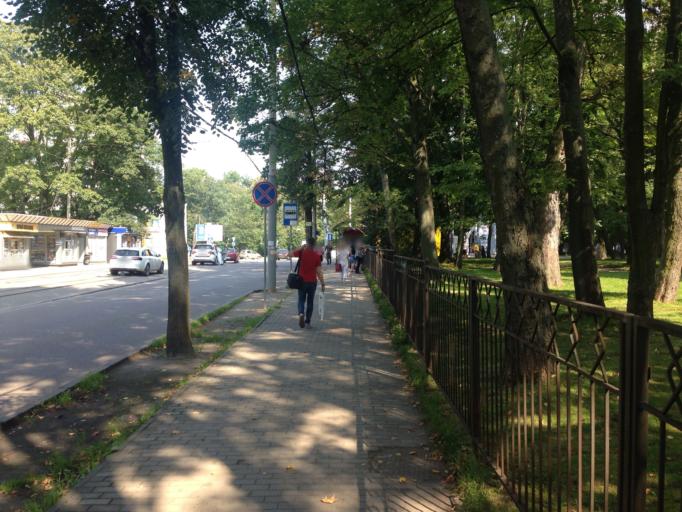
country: RU
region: Kaliningrad
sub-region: Gorod Kaliningrad
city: Kaliningrad
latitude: 54.7196
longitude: 20.4749
